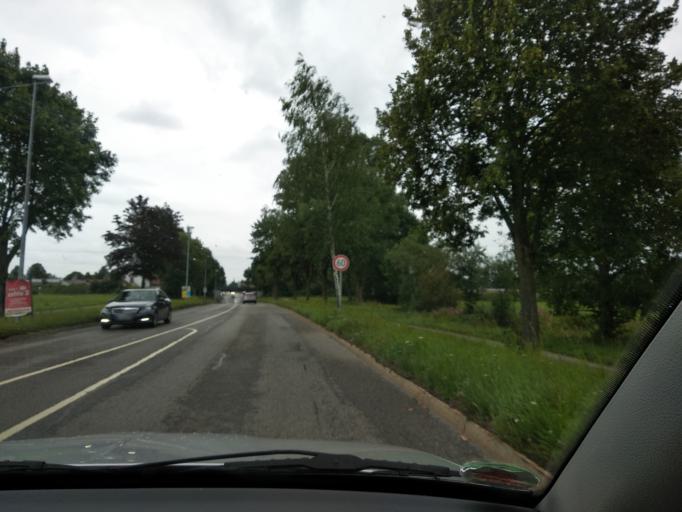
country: DE
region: Baden-Wuerttemberg
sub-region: Tuebingen Region
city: Leutkirch im Allgau
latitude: 47.8255
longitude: 10.0059
